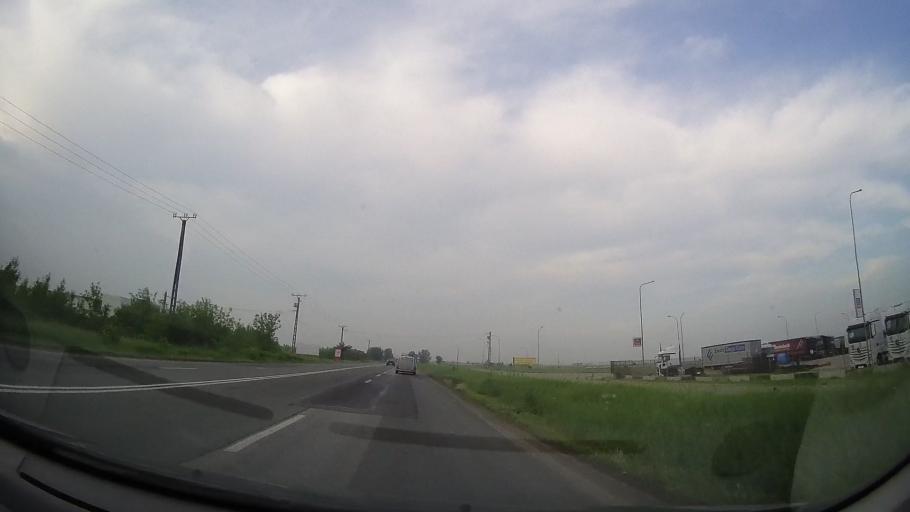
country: RO
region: Timis
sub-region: Comuna Giroc
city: Chisoda
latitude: 45.6952
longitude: 21.1776
